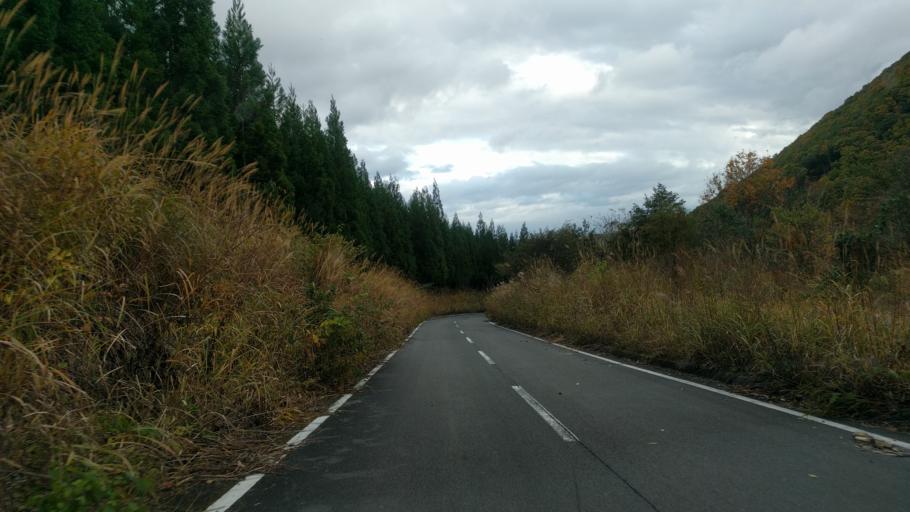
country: JP
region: Fukushima
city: Kitakata
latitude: 37.3812
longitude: 139.7069
